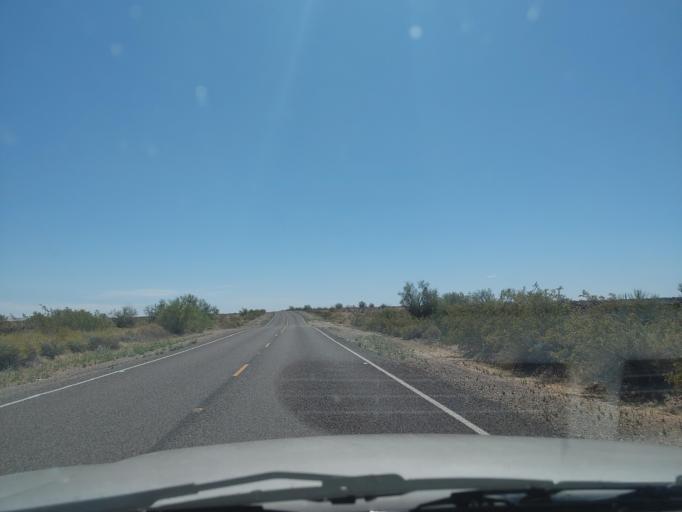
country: US
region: Arizona
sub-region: Maricopa County
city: Gila Bend
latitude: 32.9269
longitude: -113.2936
